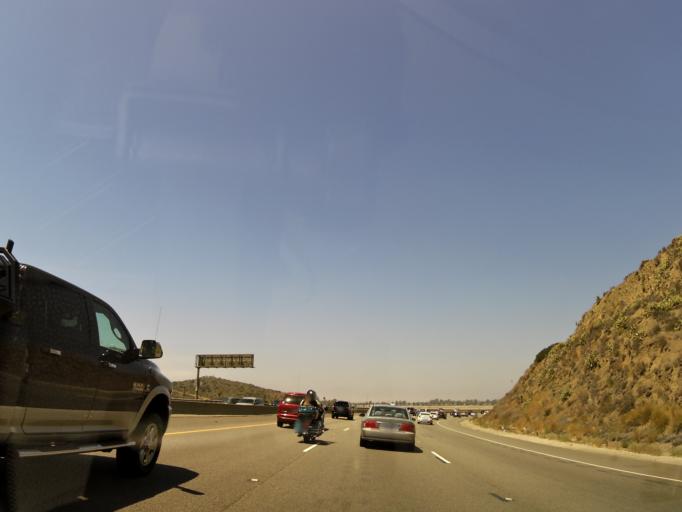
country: US
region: California
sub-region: Ventura County
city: Casa Conejo
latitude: 34.2054
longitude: -118.9874
